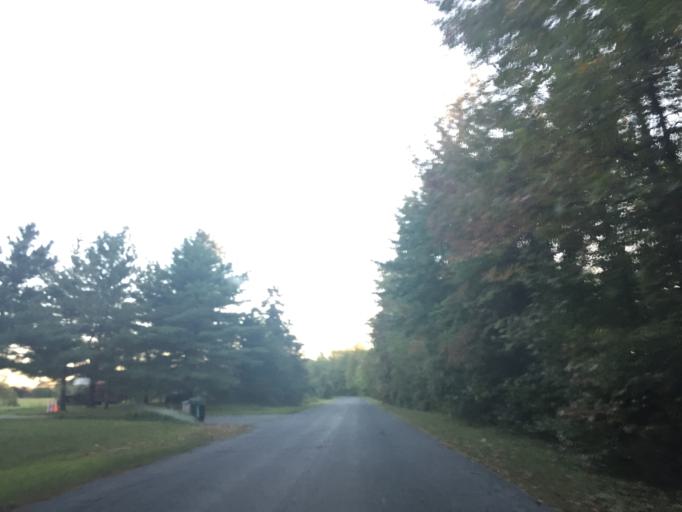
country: US
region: Maryland
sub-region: Baltimore County
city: Kingsville
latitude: 39.4256
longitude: -76.3910
